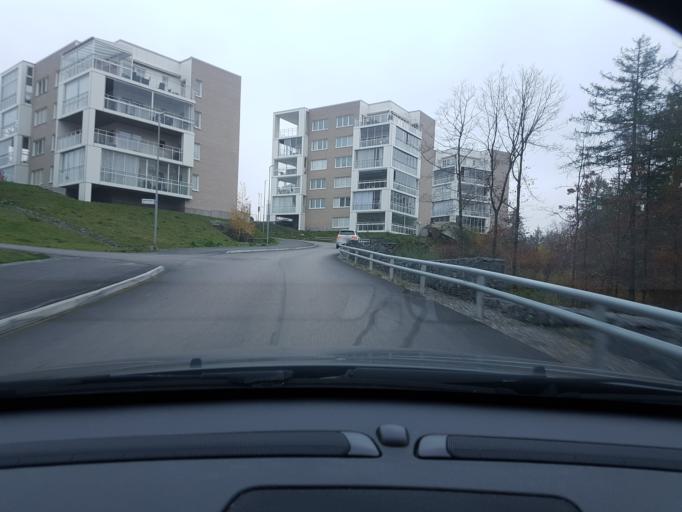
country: SE
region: Vaestra Goetaland
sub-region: Ale Kommun
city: Surte
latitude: 57.8172
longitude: 12.0252
